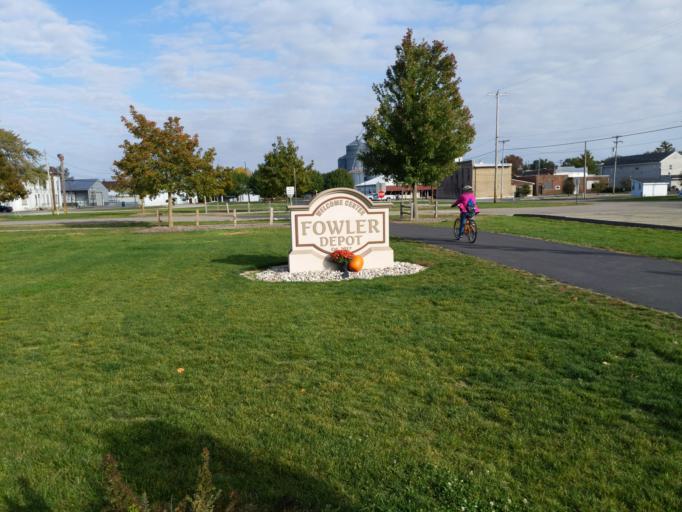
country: US
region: Michigan
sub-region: Clinton County
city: Fowler
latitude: 43.0031
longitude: -84.7415
